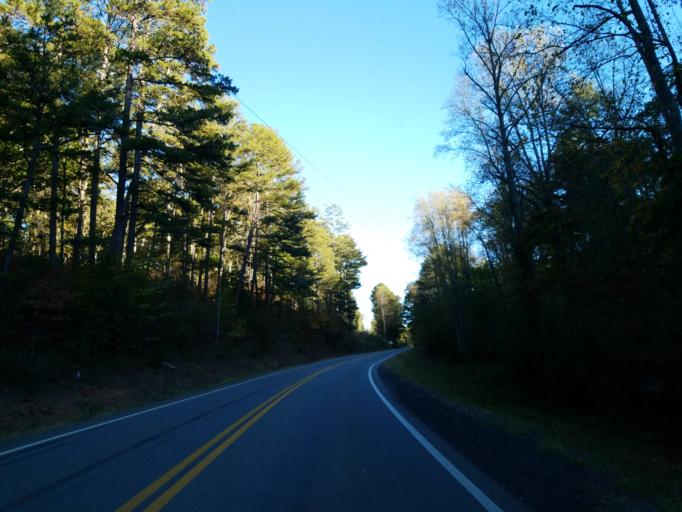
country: US
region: Georgia
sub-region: Dawson County
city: Dawsonville
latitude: 34.4253
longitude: -84.2101
